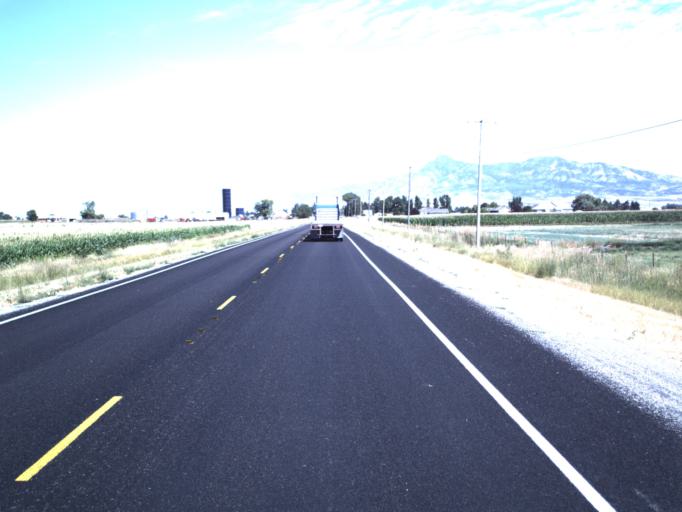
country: US
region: Utah
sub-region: Box Elder County
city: Garland
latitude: 41.7639
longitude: -112.1487
